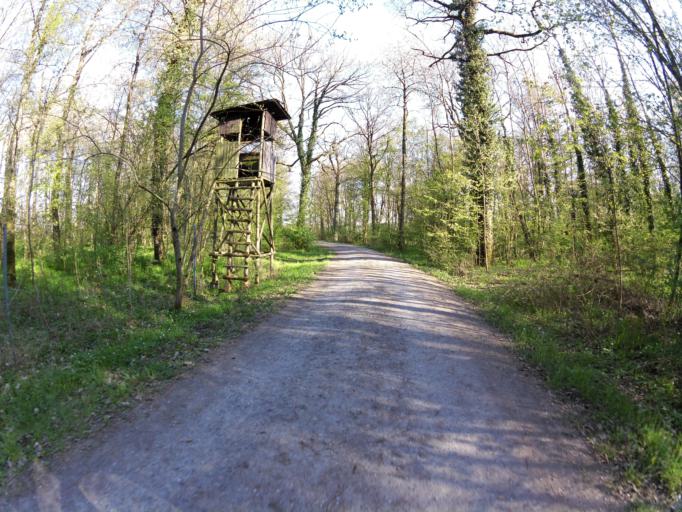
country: DE
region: Bavaria
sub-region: Regierungsbezirk Unterfranken
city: Estenfeld
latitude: 49.8640
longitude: 9.9970
